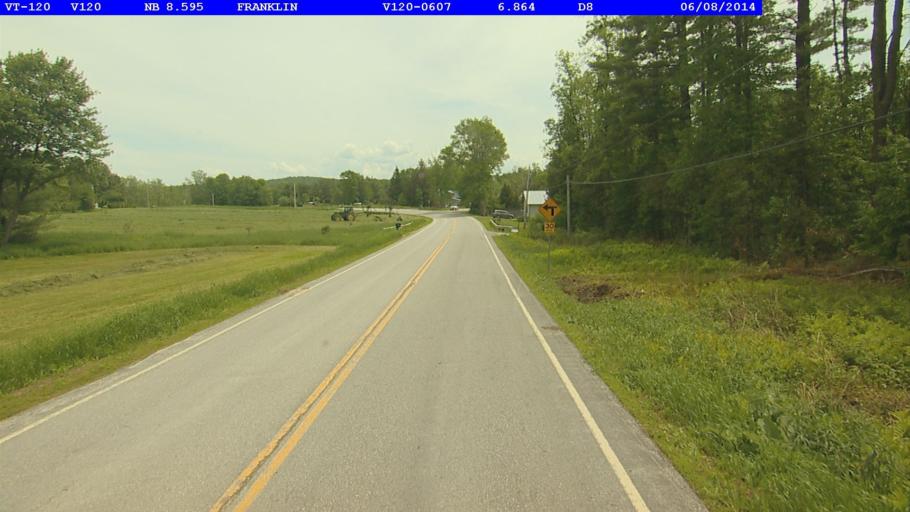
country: US
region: Vermont
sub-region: Franklin County
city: Enosburg Falls
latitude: 44.9873
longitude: -72.8582
